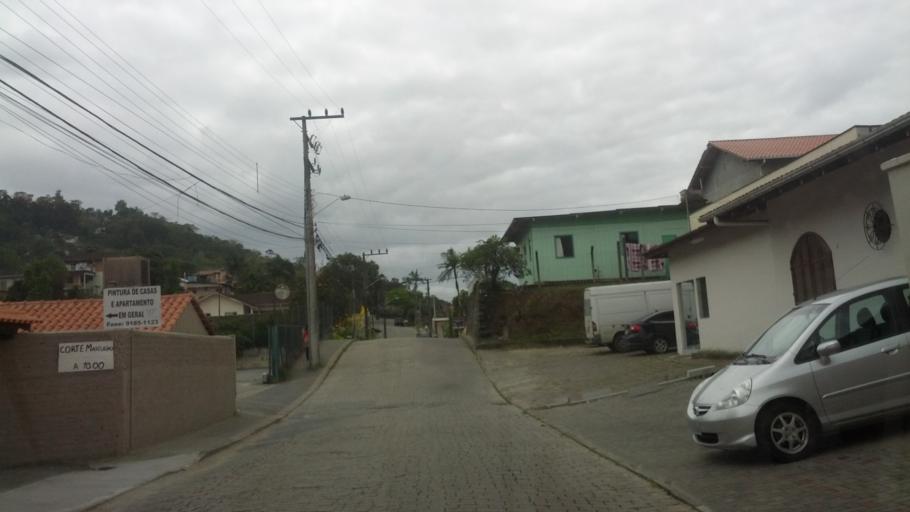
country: BR
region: Santa Catarina
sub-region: Blumenau
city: Blumenau
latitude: -26.9105
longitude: -49.1123
